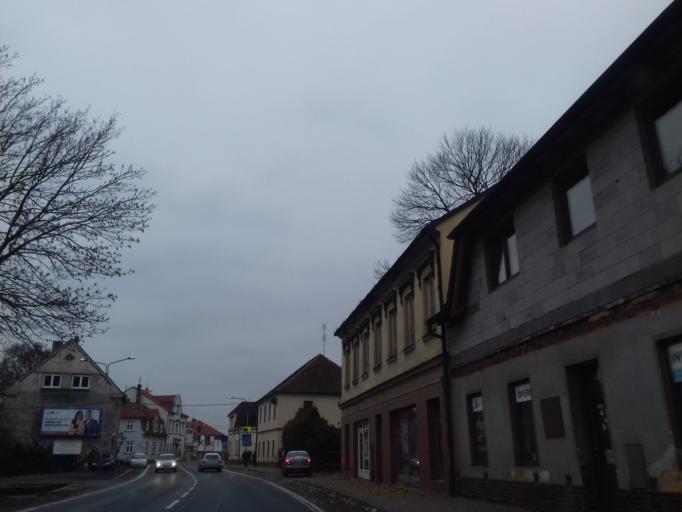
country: CZ
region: Plzensky
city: Stod
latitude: 49.6420
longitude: 13.1659
